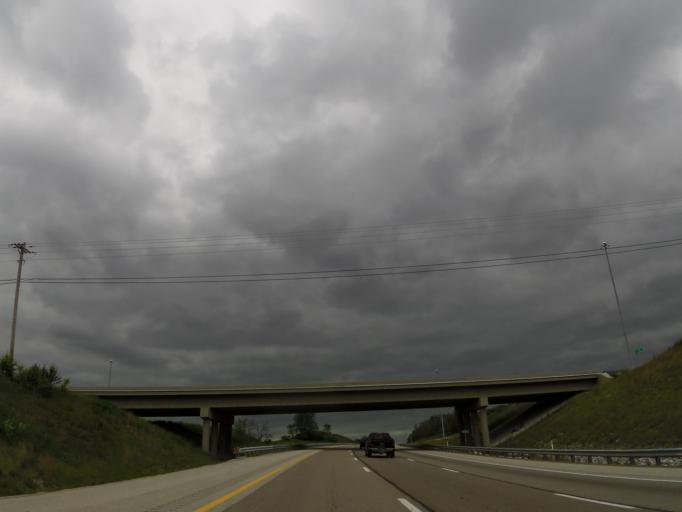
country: US
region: Kentucky
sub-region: Grant County
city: Williamstown
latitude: 38.4894
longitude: -84.5859
